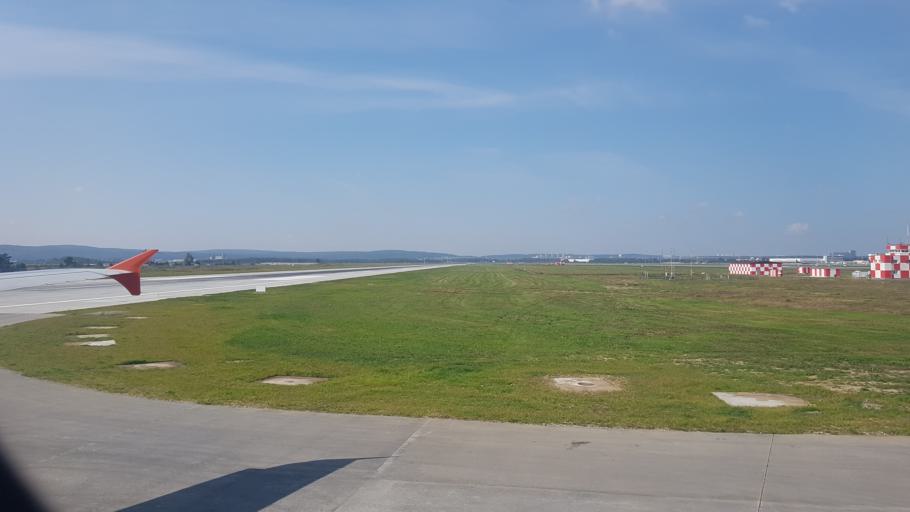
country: RU
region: Sverdlovsk
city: Aramil
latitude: 56.7409
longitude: 60.8216
